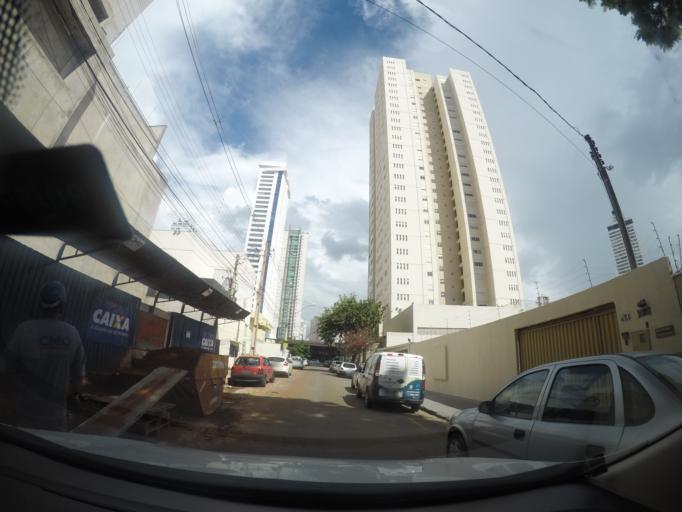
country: BR
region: Goias
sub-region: Goiania
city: Goiania
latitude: -16.7044
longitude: -49.2739
